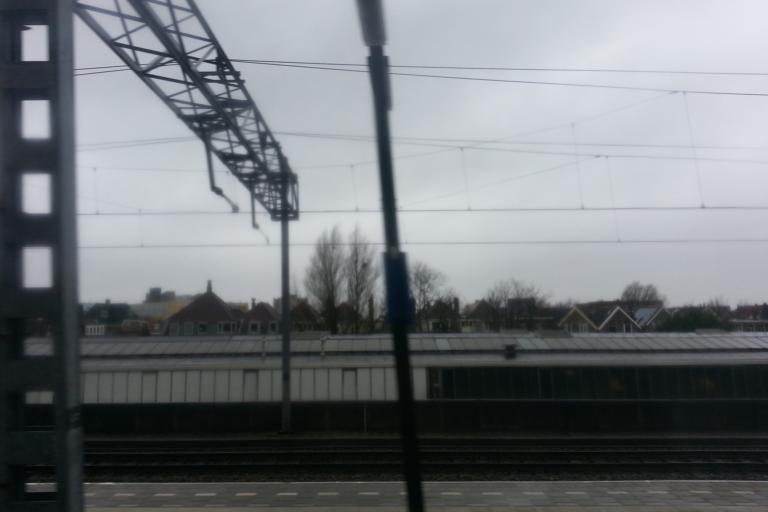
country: NL
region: South Holland
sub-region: Gemeente Leiden
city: Leiden
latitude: 52.1683
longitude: 4.4845
